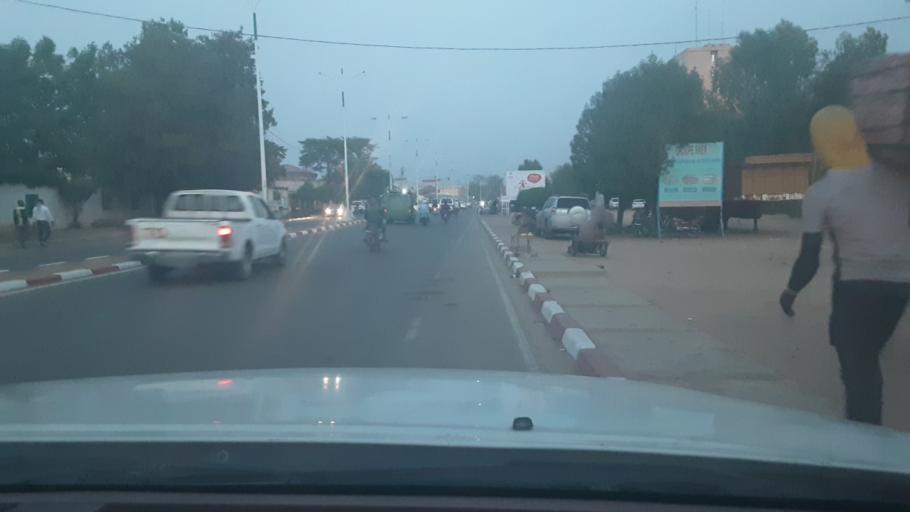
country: TD
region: Chari-Baguirmi
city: N'Djamena
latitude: 12.0950
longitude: 15.0700
